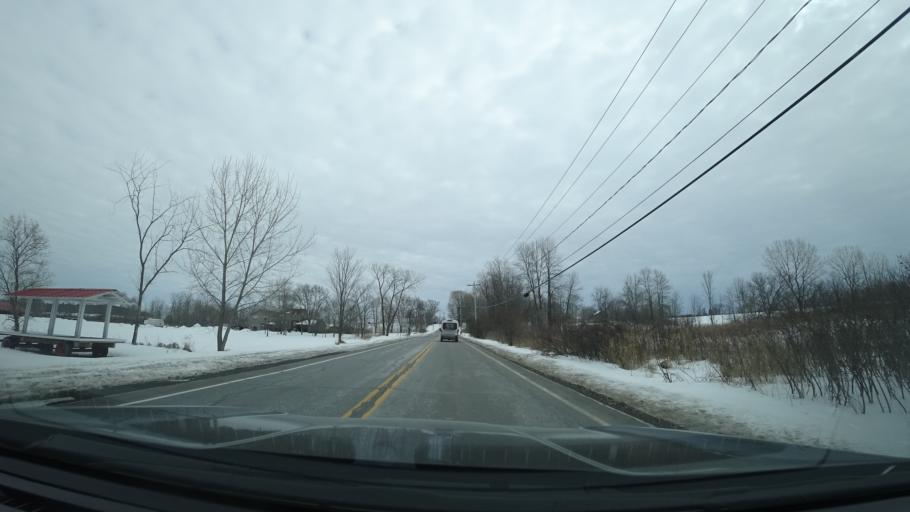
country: US
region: New York
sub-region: Washington County
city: Fort Edward
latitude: 43.2629
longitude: -73.5721
